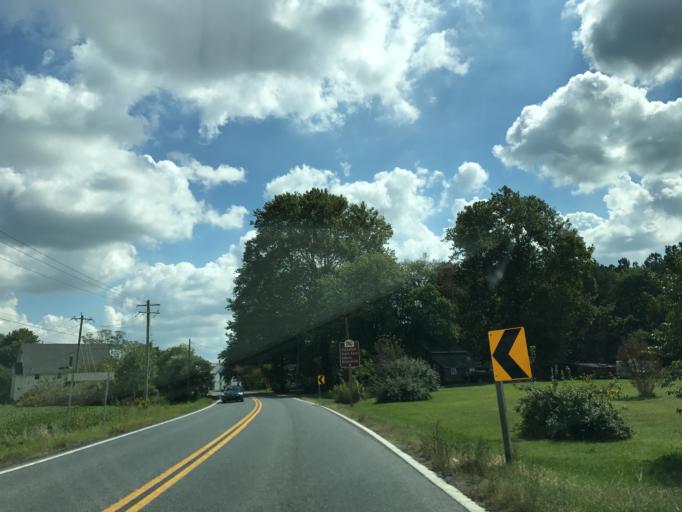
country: US
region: Maryland
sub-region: Caroline County
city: Ridgely
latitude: 39.0038
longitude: -75.9608
